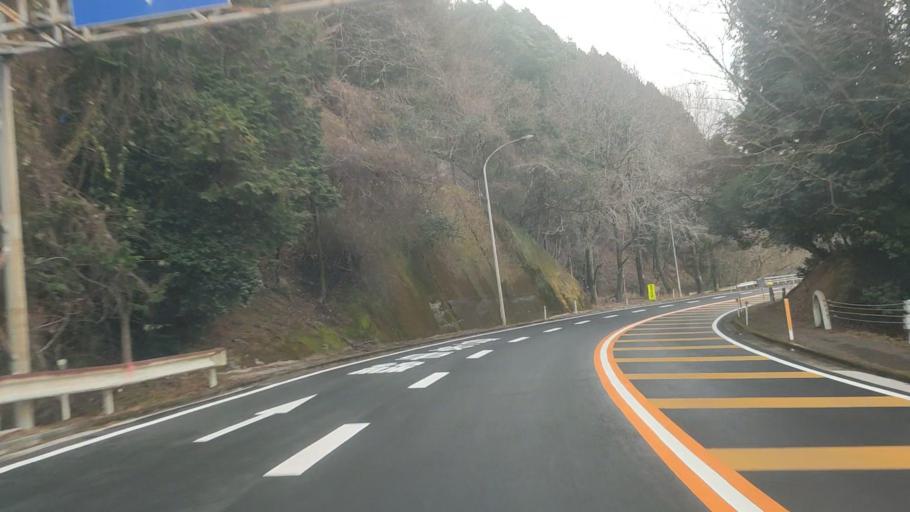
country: JP
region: Kumamoto
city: Hitoyoshi
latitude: 32.1205
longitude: 130.8147
